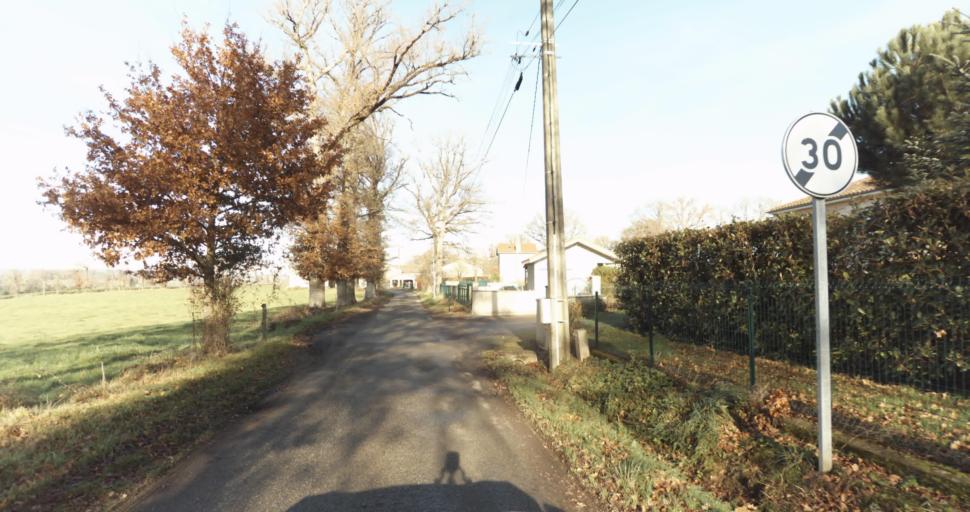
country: FR
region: Limousin
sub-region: Departement de la Haute-Vienne
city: Aixe-sur-Vienne
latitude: 45.7843
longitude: 1.1161
